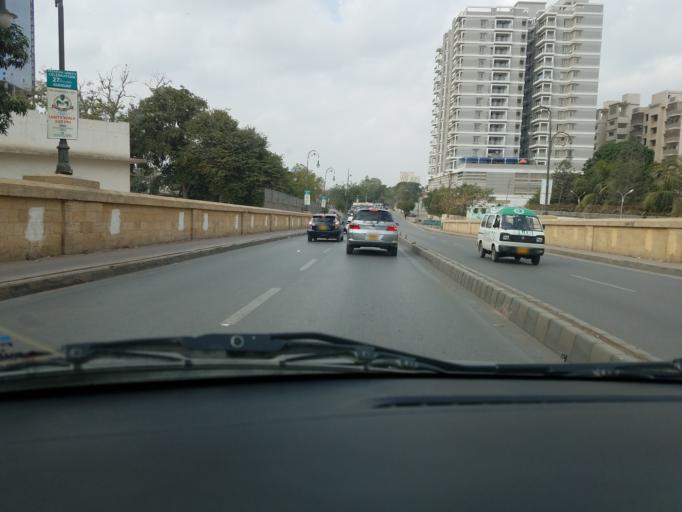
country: PK
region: Sindh
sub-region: Karachi District
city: Karachi
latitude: 24.8416
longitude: 67.0326
